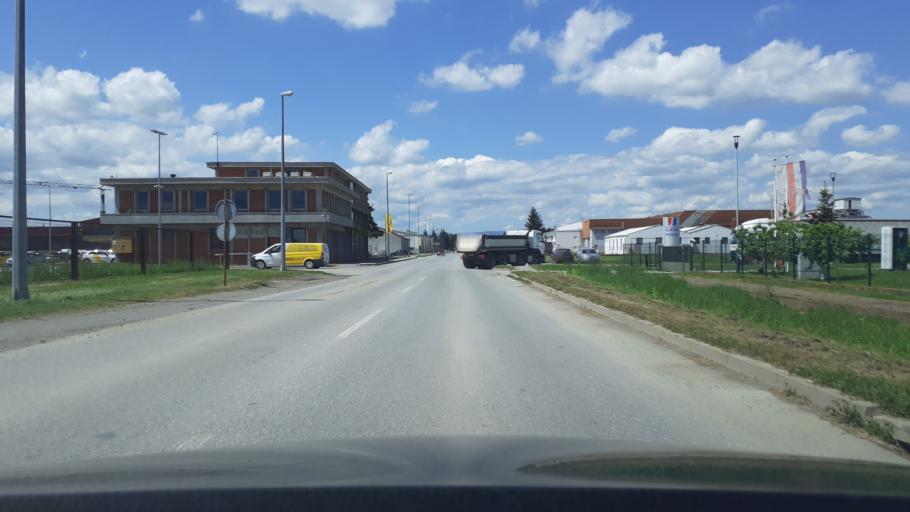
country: HR
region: Pozesko-Slavonska
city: Pozega
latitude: 45.3387
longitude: 17.6974
